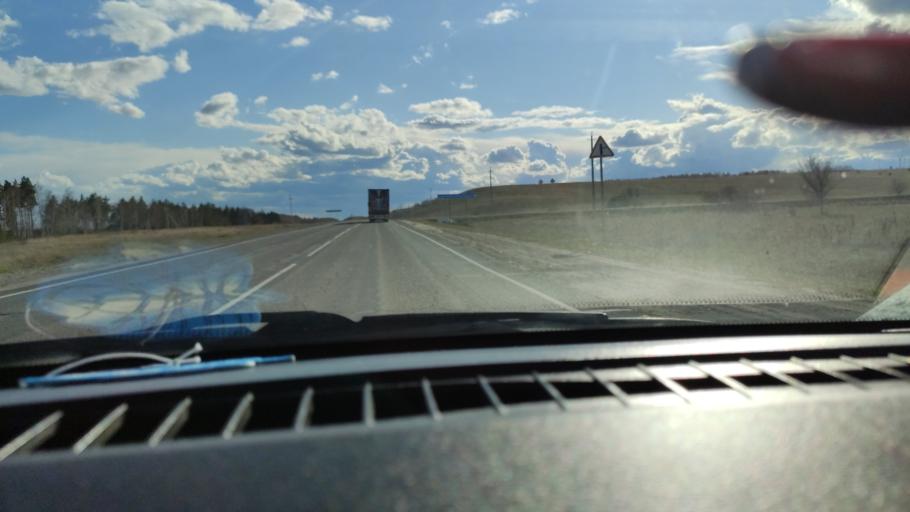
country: RU
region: Saratov
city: Sinodskoye
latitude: 52.0748
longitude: 46.7851
